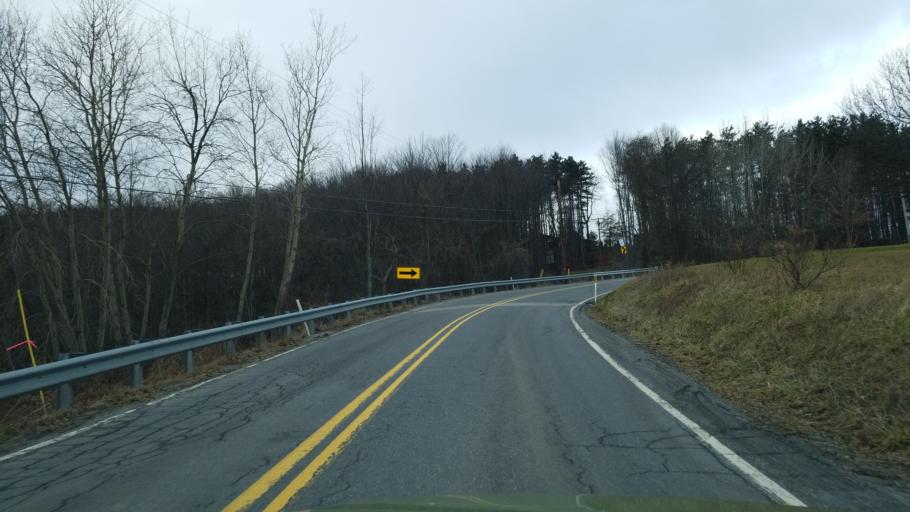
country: US
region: Pennsylvania
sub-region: Clearfield County
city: Hyde
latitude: 41.0382
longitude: -78.4901
